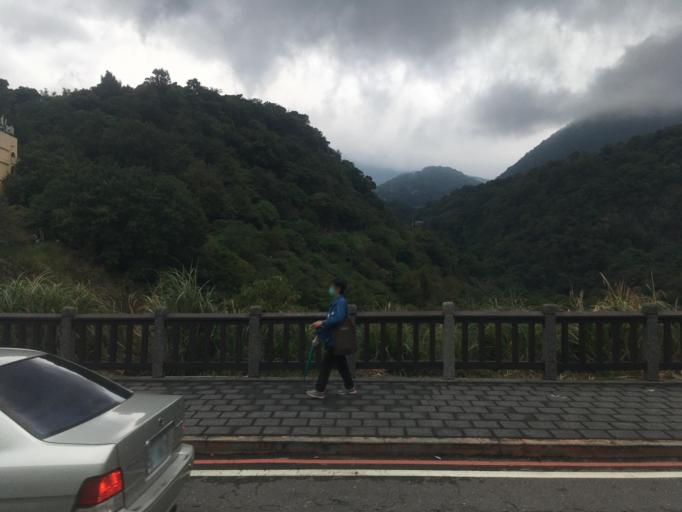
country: TW
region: Taipei
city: Taipei
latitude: 25.1437
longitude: 121.5270
